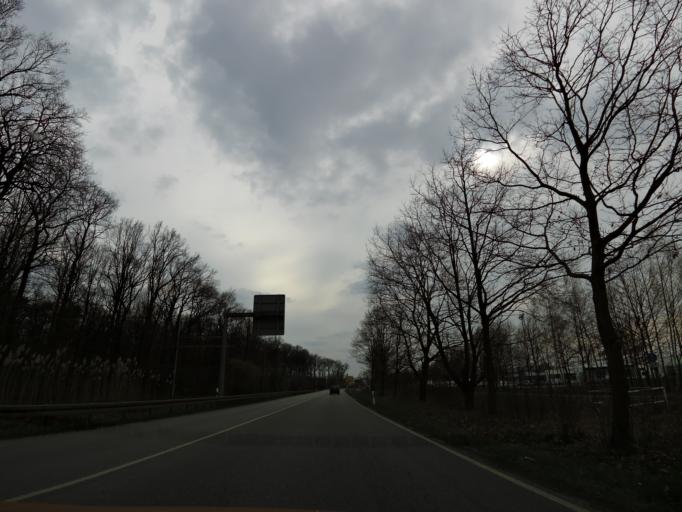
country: DE
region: Brandenburg
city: Frankfurt (Oder)
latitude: 52.3058
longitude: 14.4845
